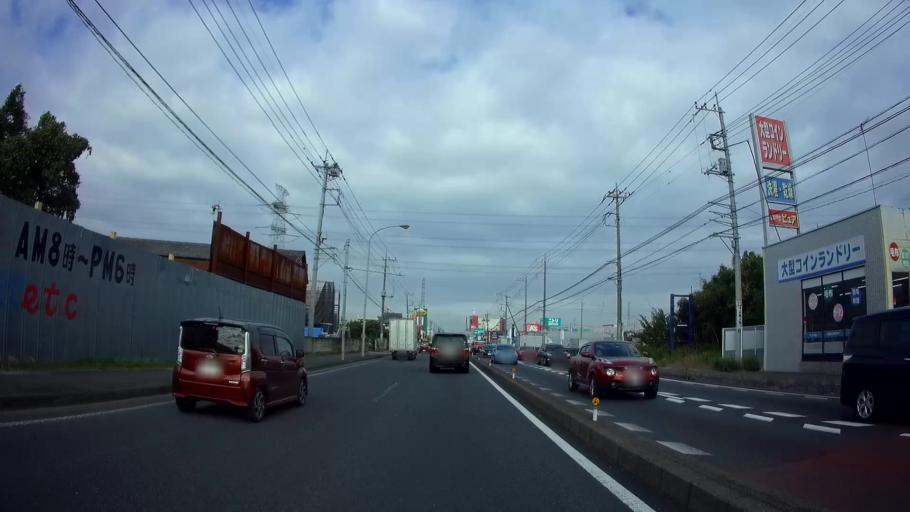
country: JP
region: Saitama
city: Konosu
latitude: 36.0760
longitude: 139.4949
